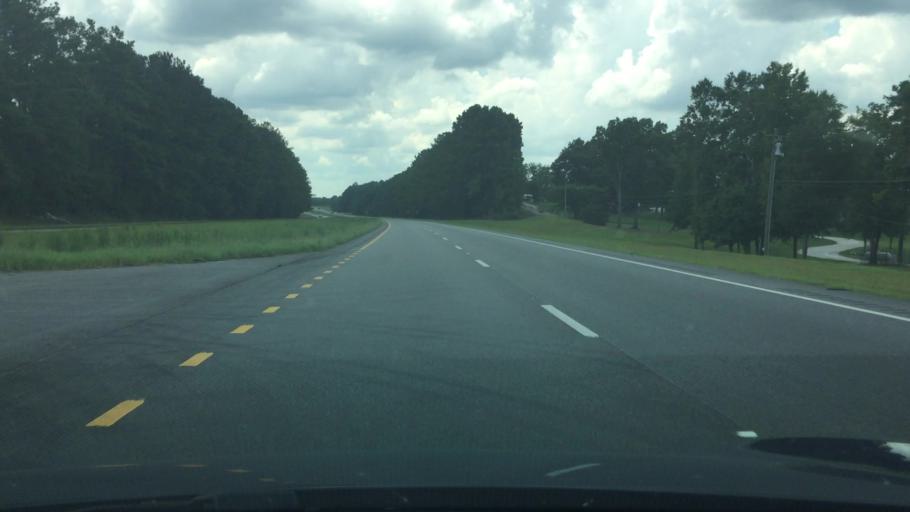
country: US
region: Alabama
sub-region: Pike County
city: Troy
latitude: 31.8960
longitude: -86.0102
